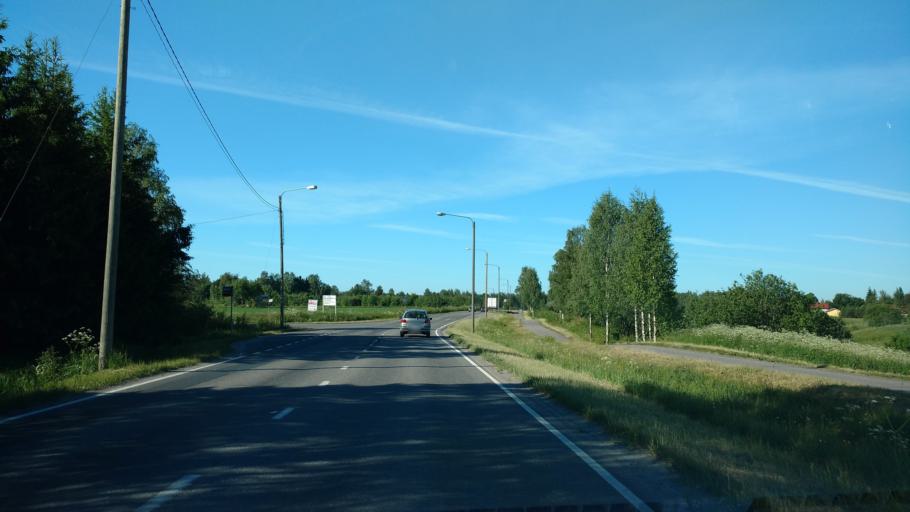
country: FI
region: Varsinais-Suomi
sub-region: Salo
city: Salo
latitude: 60.4002
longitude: 23.1603
